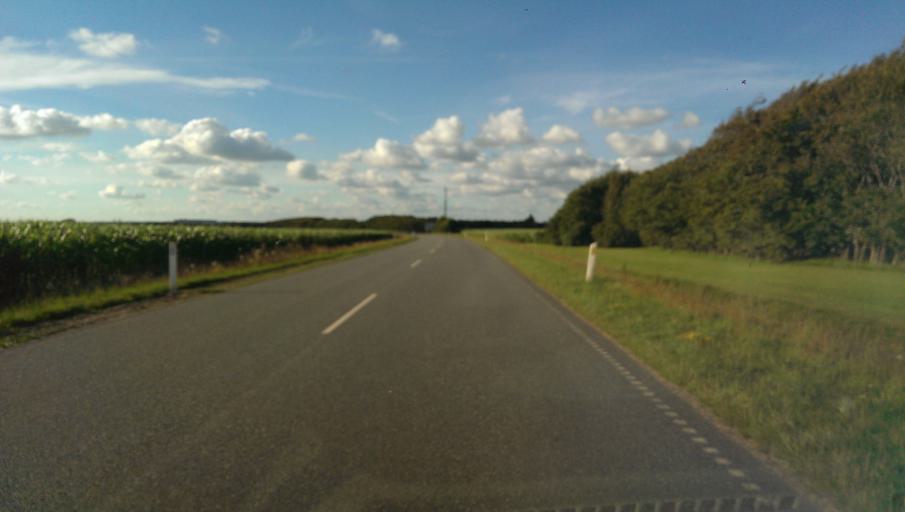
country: DK
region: South Denmark
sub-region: Esbjerg Kommune
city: Tjaereborg
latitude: 55.5145
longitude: 8.5494
